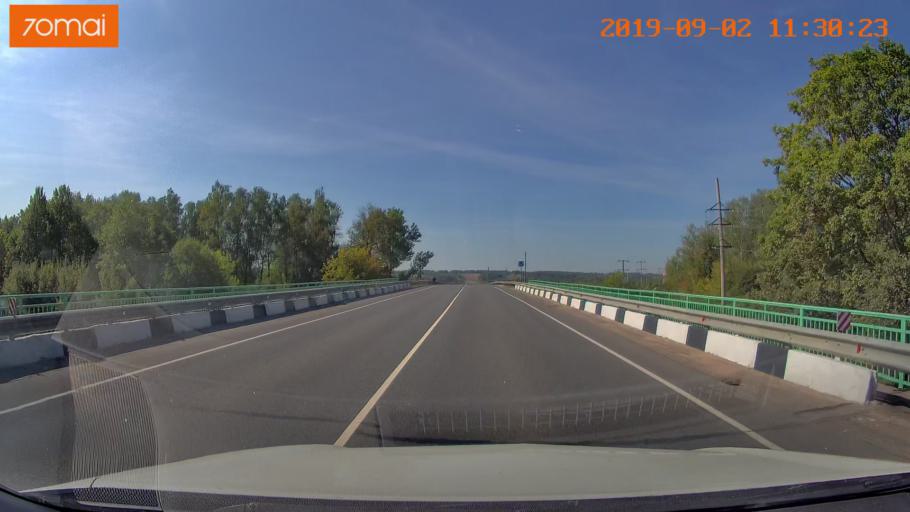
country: RU
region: Smolensk
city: Roslavl'
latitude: 53.9847
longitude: 32.8354
